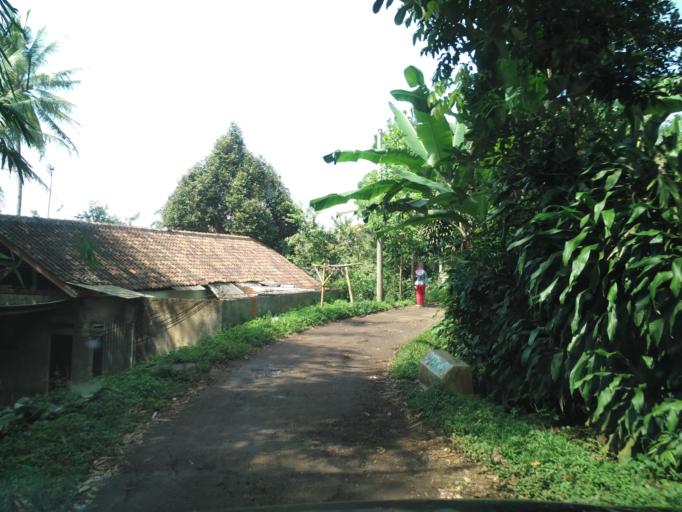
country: ID
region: West Java
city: Ciranjang-hilir
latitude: -6.7883
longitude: 107.1123
